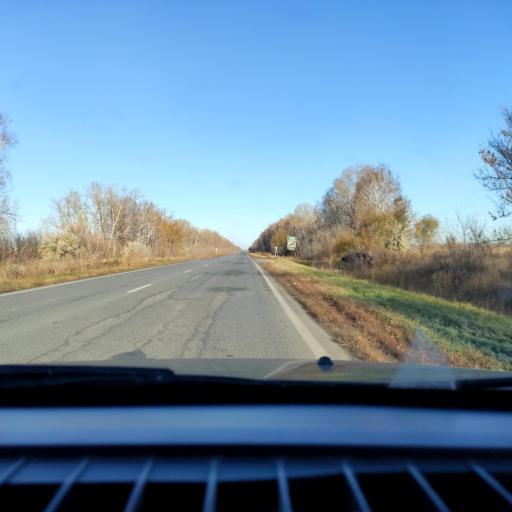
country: RU
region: Samara
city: Tol'yatti
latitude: 53.6064
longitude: 49.3189
